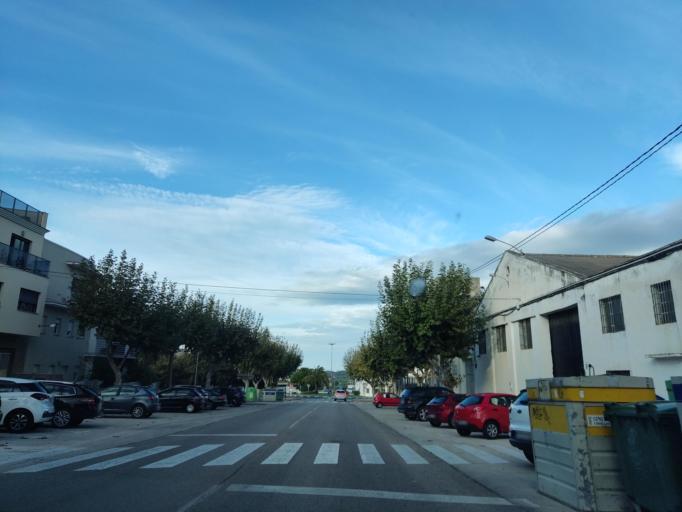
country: ES
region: Valencia
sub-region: Provincia de Alicante
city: Pego
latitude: 38.8424
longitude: -0.1107
